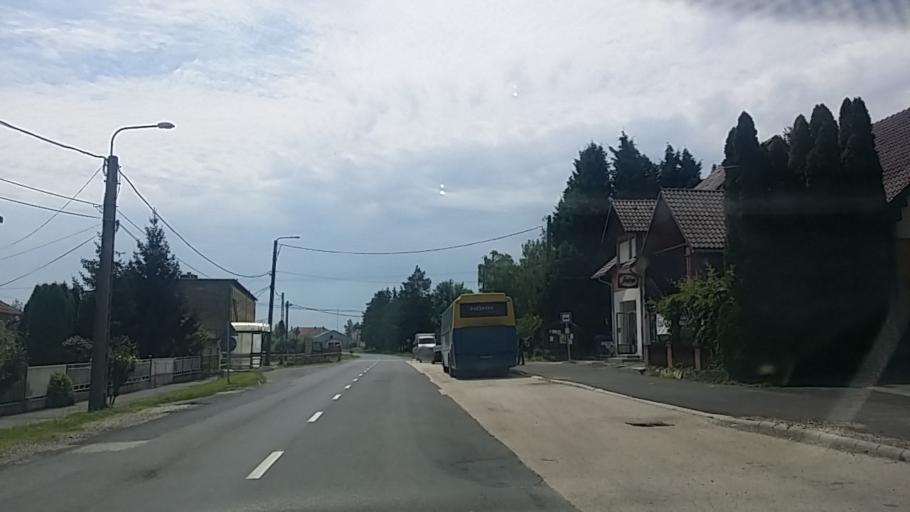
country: HU
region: Zala
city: Lenti
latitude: 46.5556
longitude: 16.5564
